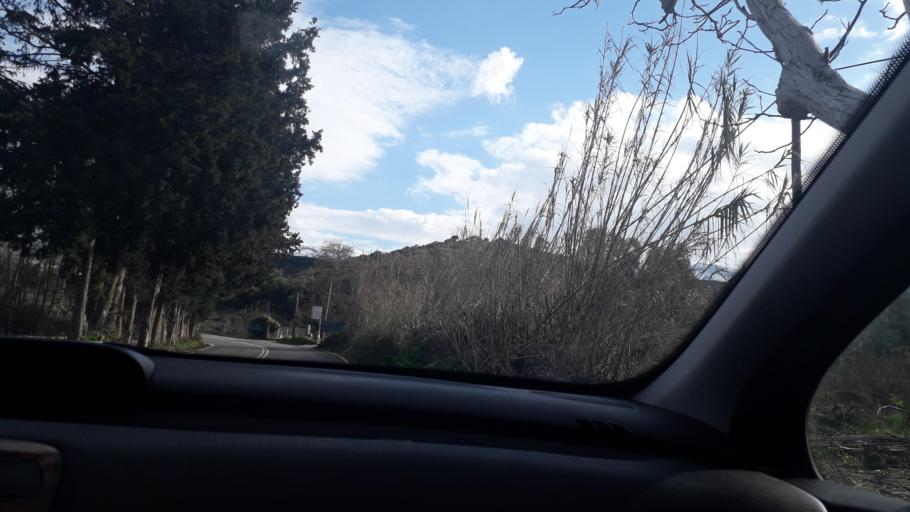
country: GR
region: Crete
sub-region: Nomos Rethymnis
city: Agia Foteini
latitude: 35.2899
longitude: 24.5611
